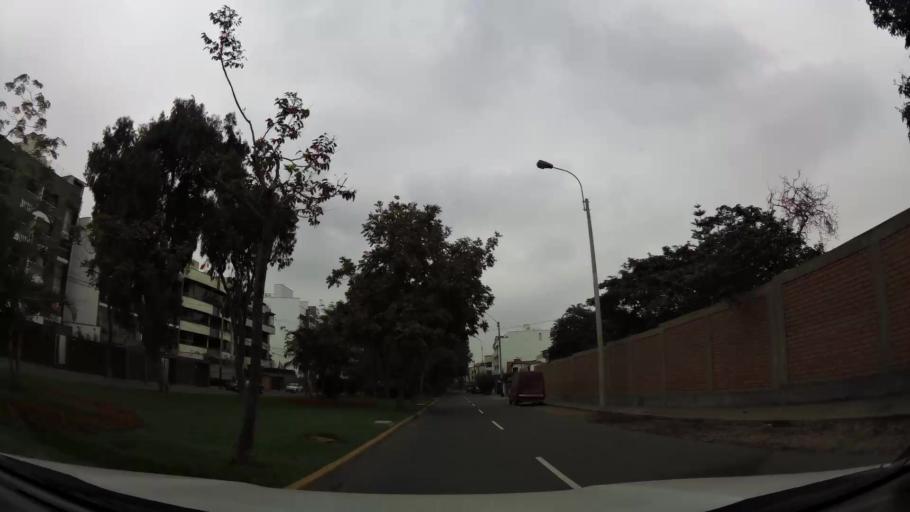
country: PE
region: Lima
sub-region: Lima
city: Surco
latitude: -12.1157
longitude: -76.9874
